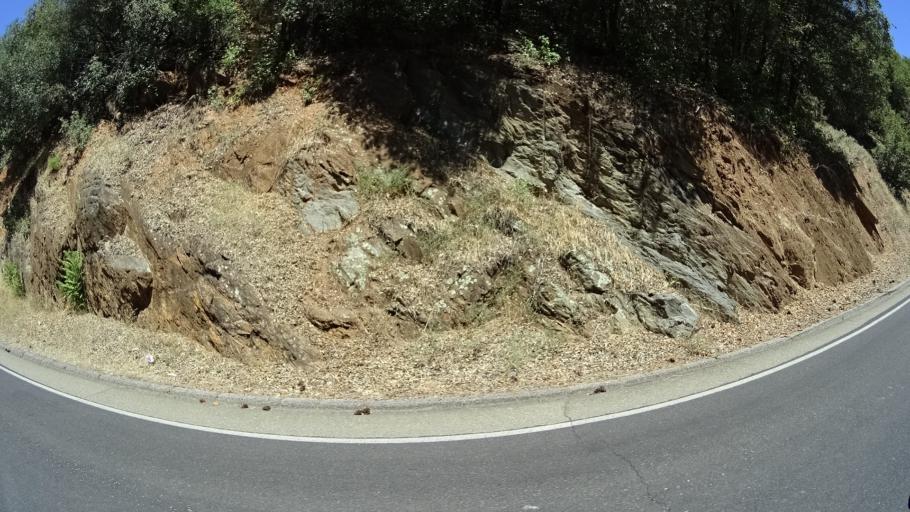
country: US
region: California
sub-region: Calaveras County
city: Murphys
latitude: 38.1337
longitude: -120.4759
